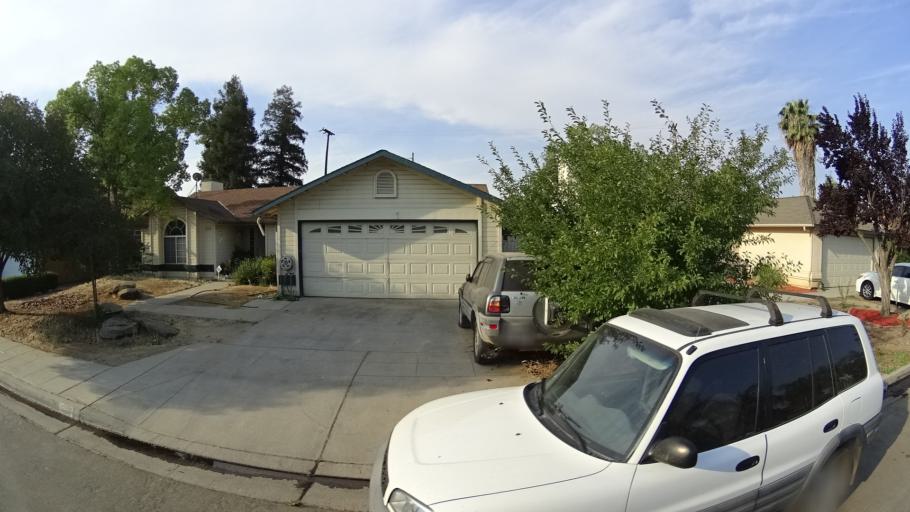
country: US
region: California
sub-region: Fresno County
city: West Park
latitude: 36.7686
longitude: -119.8546
